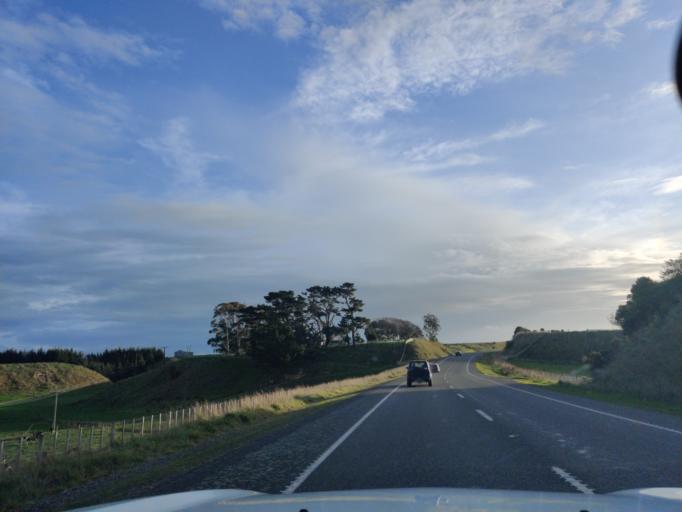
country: NZ
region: Manawatu-Wanganui
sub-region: Horowhenua District
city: Foxton
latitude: -40.5126
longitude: 175.4640
